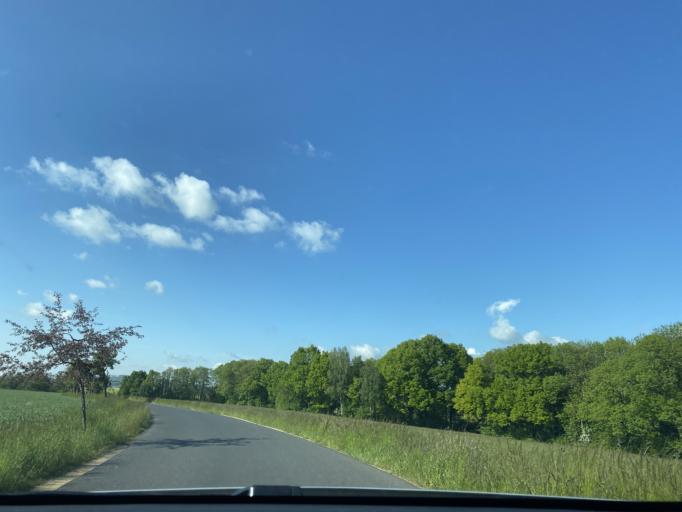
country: DE
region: Saxony
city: Reichenbach
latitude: 51.1133
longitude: 14.8344
